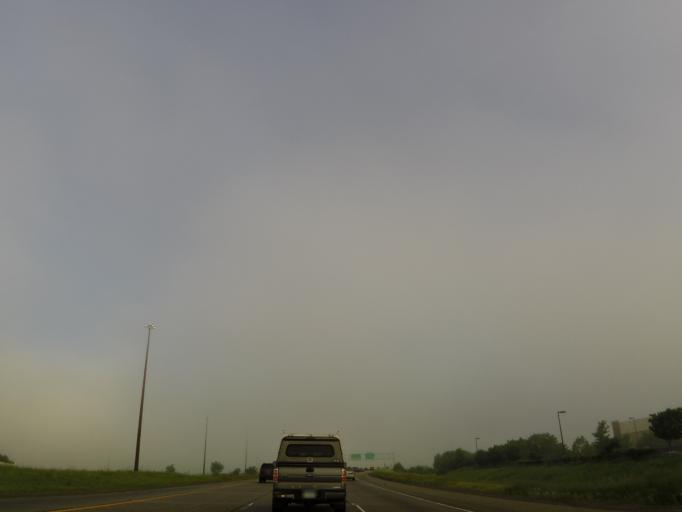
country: US
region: Minnesota
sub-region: Hennepin County
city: Maple Grove
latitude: 45.0910
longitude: -93.4391
